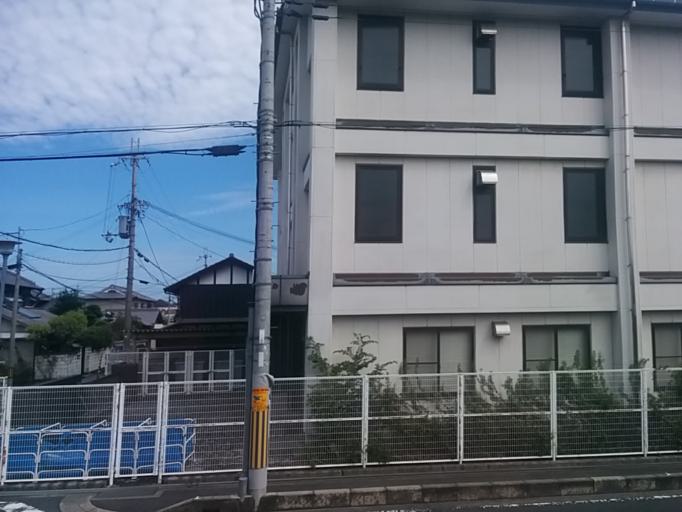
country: JP
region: Nara
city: Kashihara-shi
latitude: 34.4901
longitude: 135.7945
